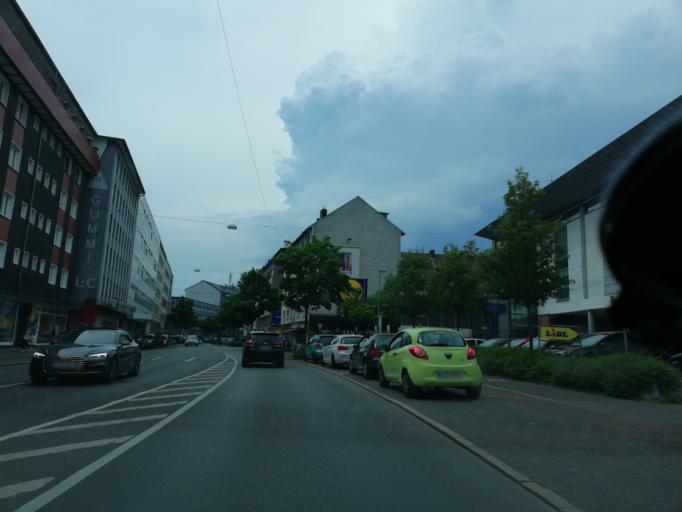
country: DE
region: North Rhine-Westphalia
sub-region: Regierungsbezirk Dusseldorf
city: Wuppertal
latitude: 51.2576
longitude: 7.1571
